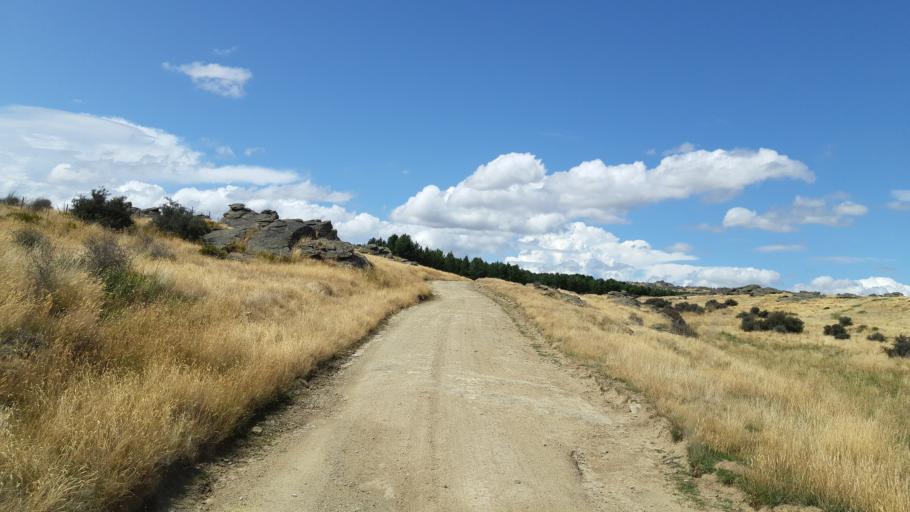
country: NZ
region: Otago
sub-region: Queenstown-Lakes District
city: Wanaka
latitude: -45.2654
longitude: 169.7137
